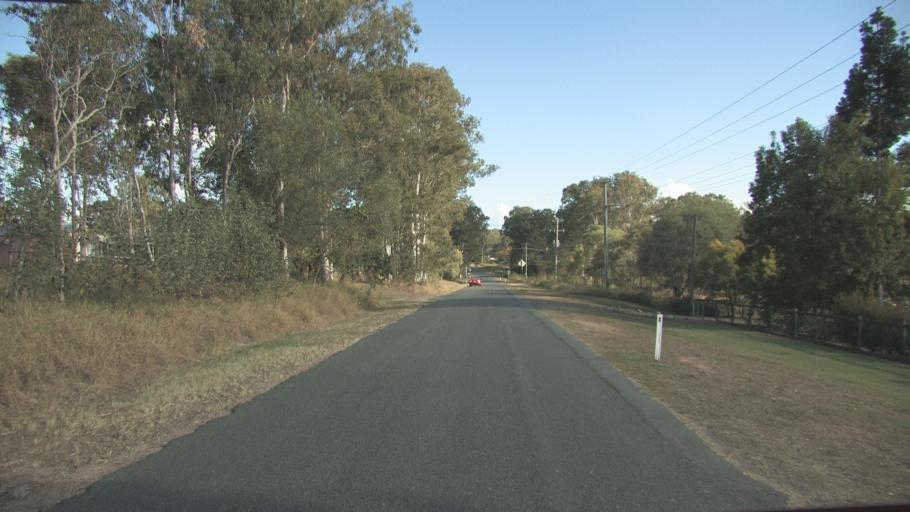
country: AU
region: Queensland
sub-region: Ipswich
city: Springfield Lakes
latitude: -27.7363
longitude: 152.9444
